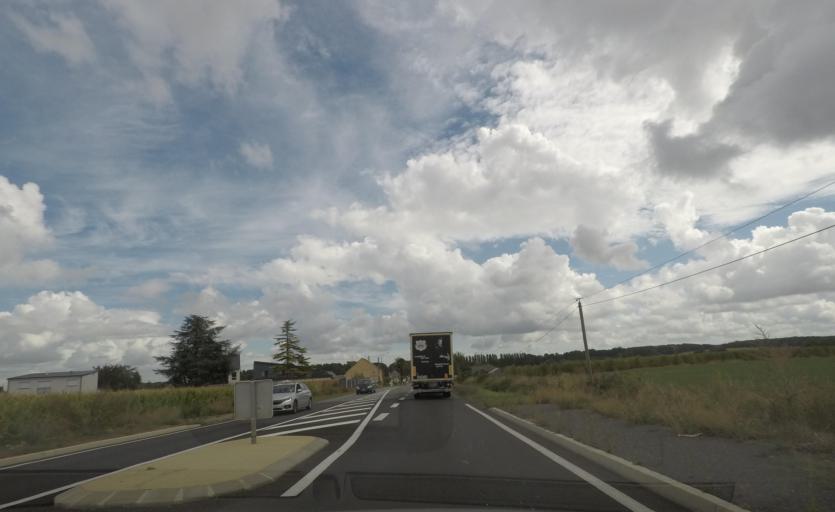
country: FR
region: Pays de la Loire
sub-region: Departement de Maine-et-Loire
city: Seiches-sur-le-Loir
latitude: 47.5671
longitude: -0.3631
